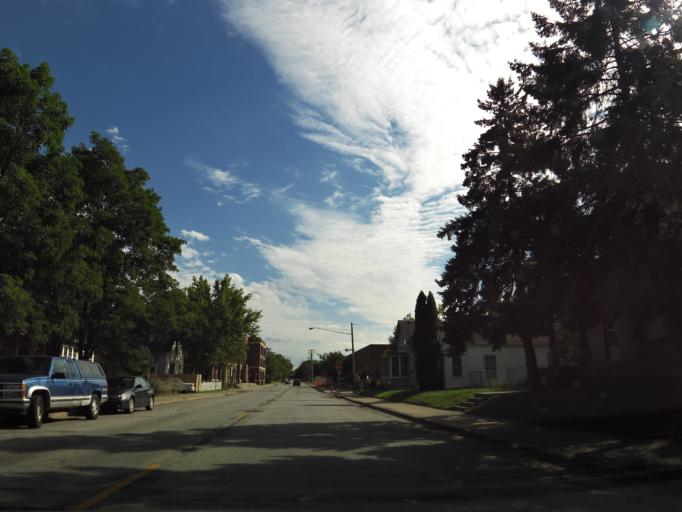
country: US
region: Minnesota
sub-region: Anoka County
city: Columbia Heights
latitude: 45.0107
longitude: -93.2526
